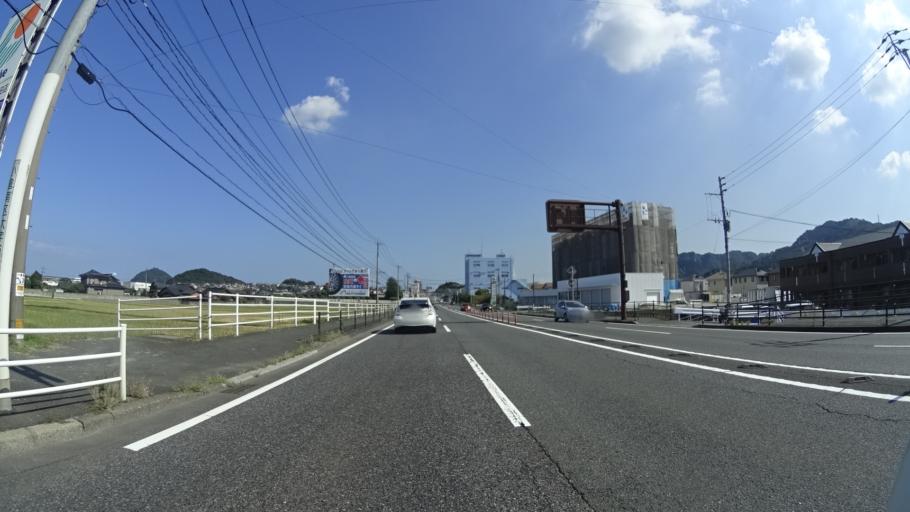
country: JP
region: Fukuoka
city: Kanda
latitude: 33.8065
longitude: 130.9594
